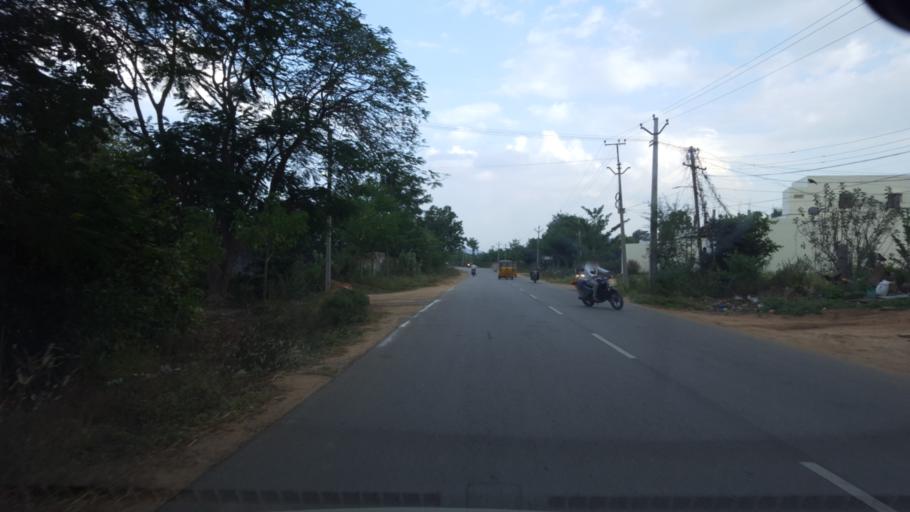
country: IN
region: Telangana
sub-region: Mahbubnagar
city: Mahbubnagar
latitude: 16.7593
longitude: 77.9609
